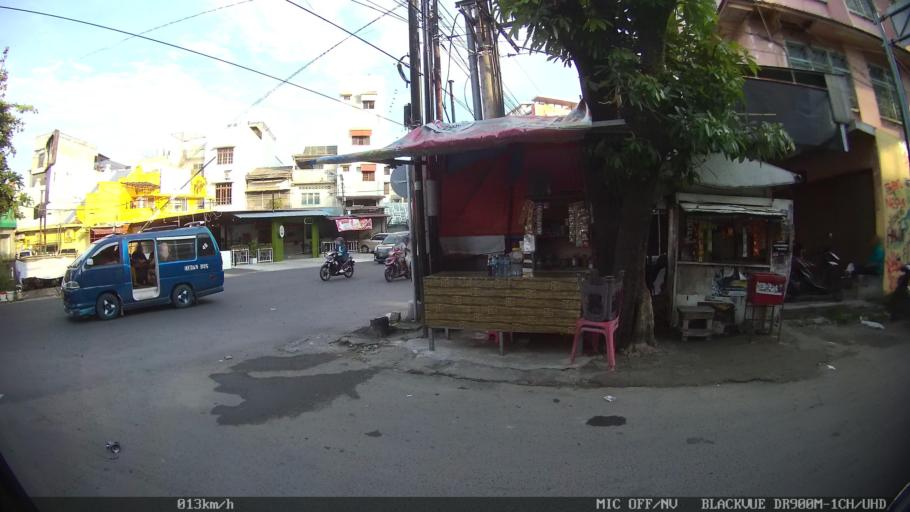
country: ID
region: North Sumatra
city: Medan
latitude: 3.5904
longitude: 98.6683
